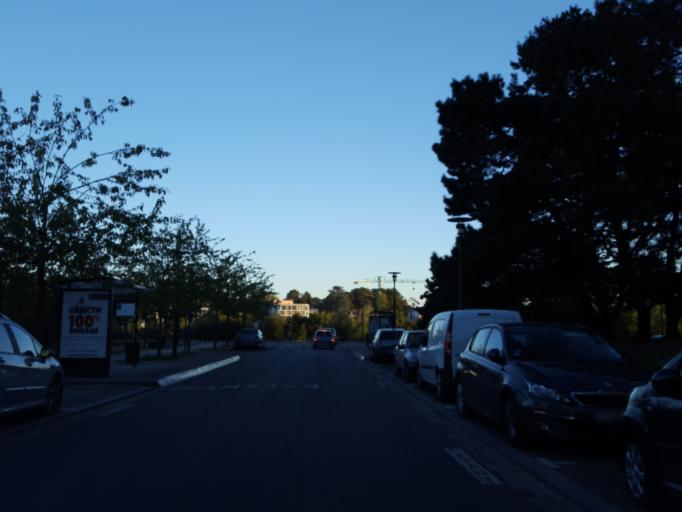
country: FR
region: Pays de la Loire
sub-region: Departement de la Loire-Atlantique
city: Nantes
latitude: 47.2052
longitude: -1.5320
